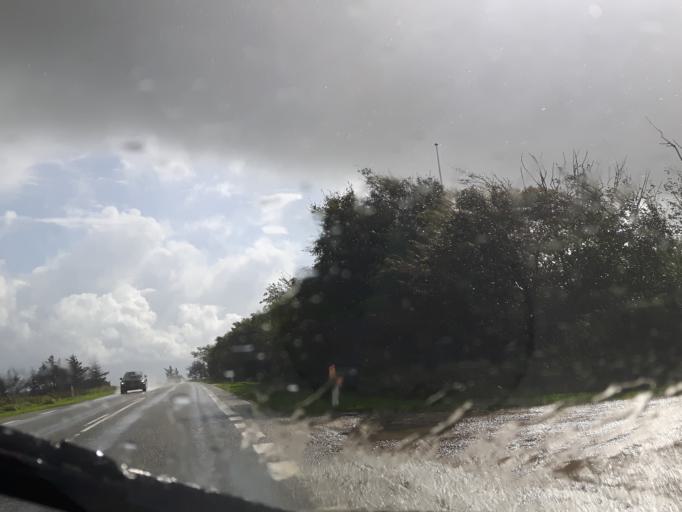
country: DK
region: Central Jutland
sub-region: Struer Kommune
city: Struer
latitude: 56.6173
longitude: 8.5220
